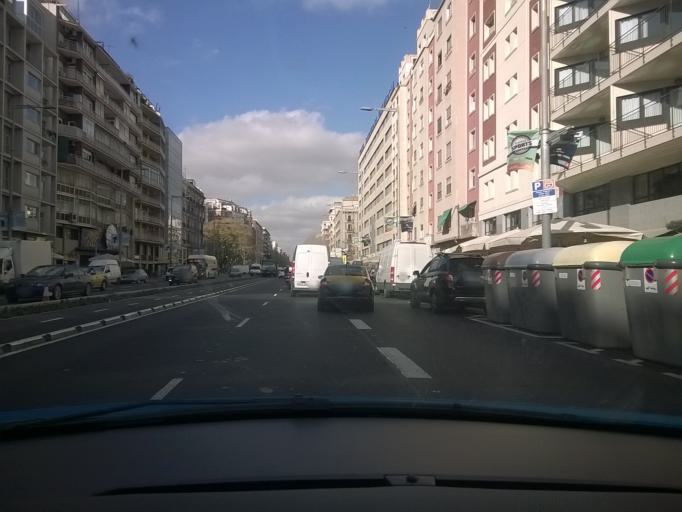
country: ES
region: Catalonia
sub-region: Provincia de Barcelona
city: Ciutat Vella
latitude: 41.3751
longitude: 2.1695
